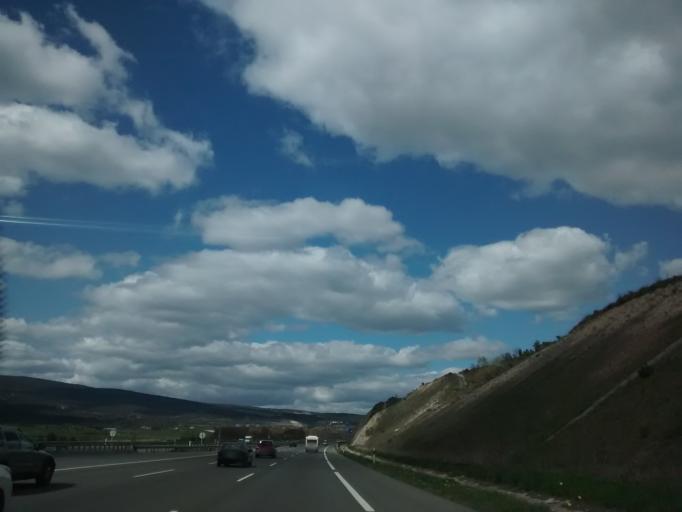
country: ES
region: Basque Country
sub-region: Provincia de Alava
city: Arminon
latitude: 42.7915
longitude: -2.8217
